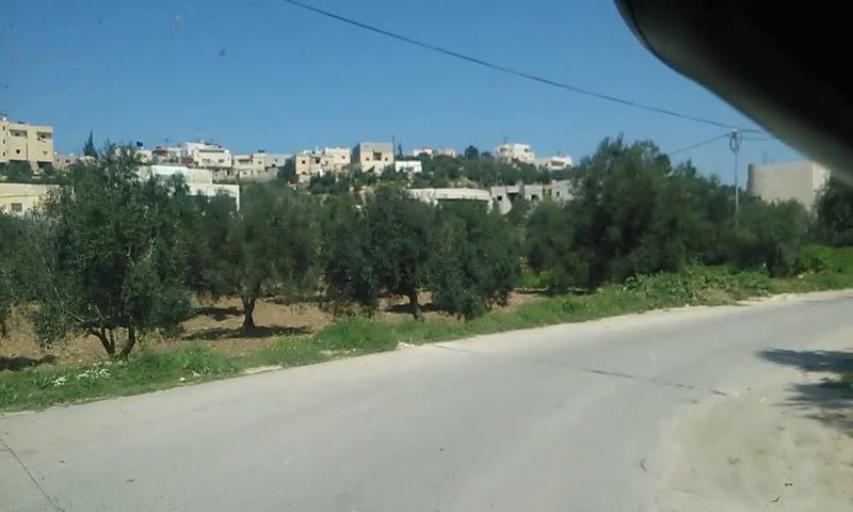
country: PS
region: West Bank
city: Al Majd
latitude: 31.4887
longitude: 34.9442
